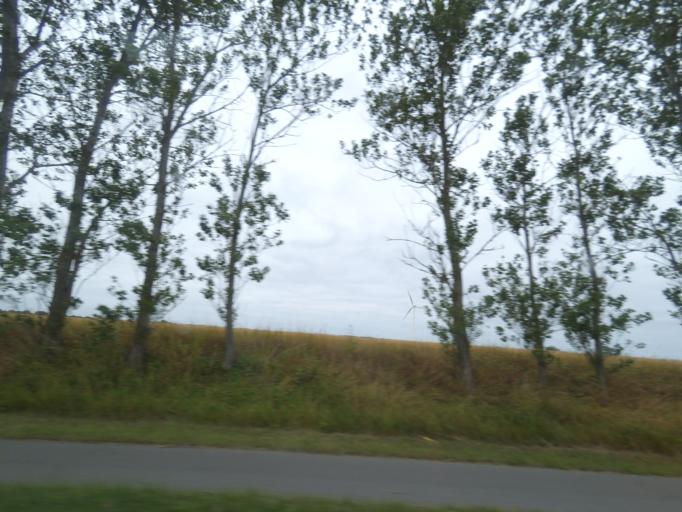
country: DK
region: South Denmark
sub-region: Nordfyns Kommune
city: Otterup
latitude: 55.5300
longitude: 10.4216
